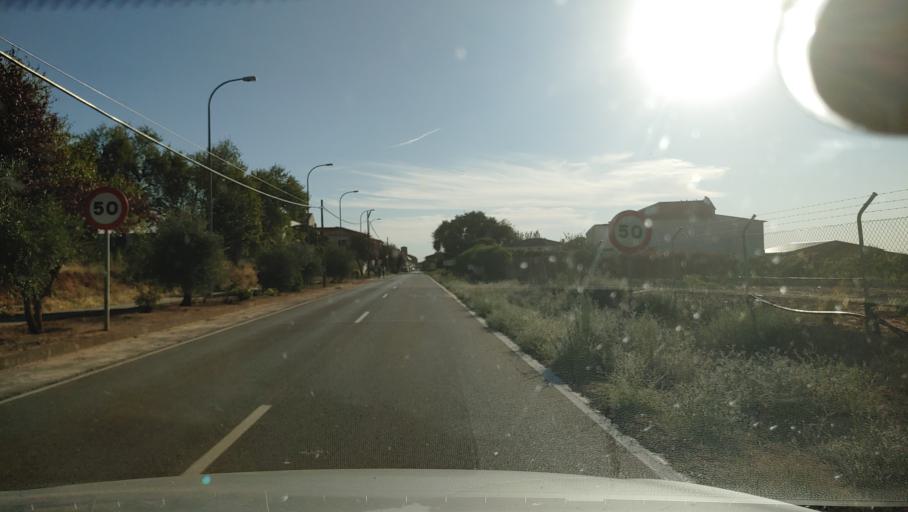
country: ES
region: Castille-La Mancha
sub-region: Provincia de Ciudad Real
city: Infantes
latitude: 38.7419
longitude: -3.0032
